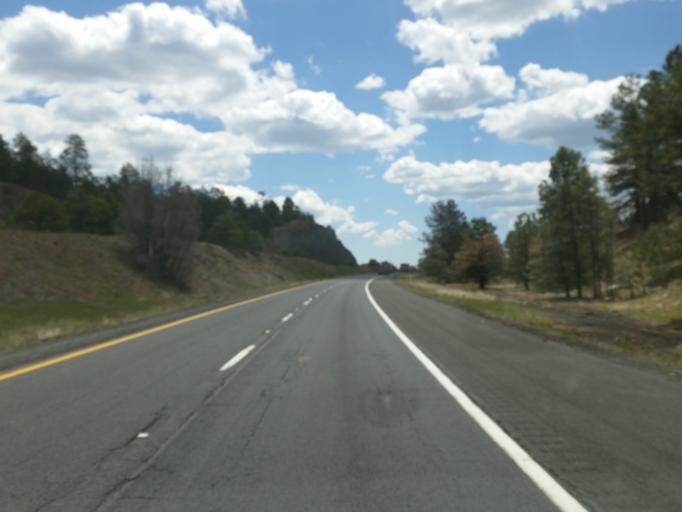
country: US
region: Arizona
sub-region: Coconino County
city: Parks
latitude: 35.2513
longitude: -111.8987
